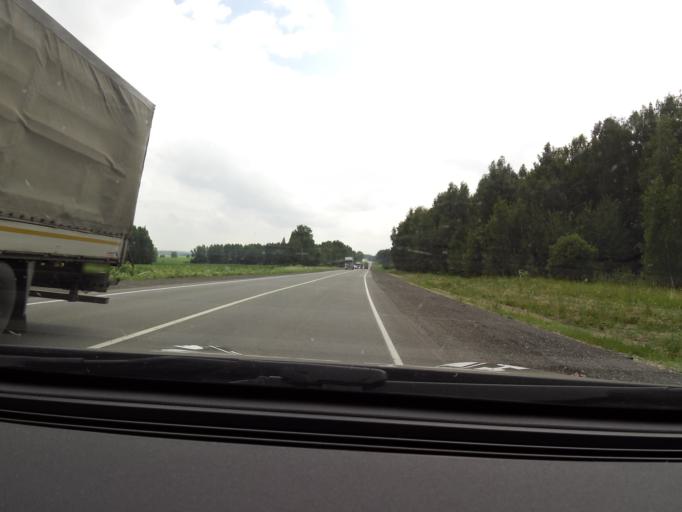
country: RU
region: Perm
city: Suksun
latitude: 56.9764
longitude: 57.5154
